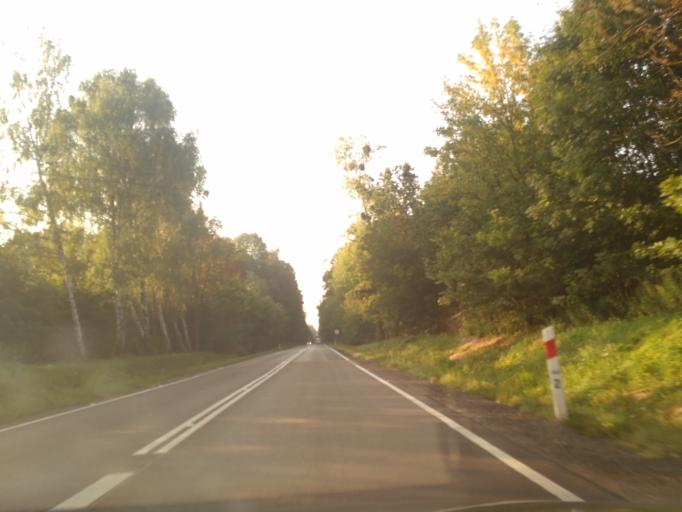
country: PL
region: Lublin Voivodeship
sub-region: Powiat krasnicki
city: Szastarka
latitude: 50.8604
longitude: 22.2802
